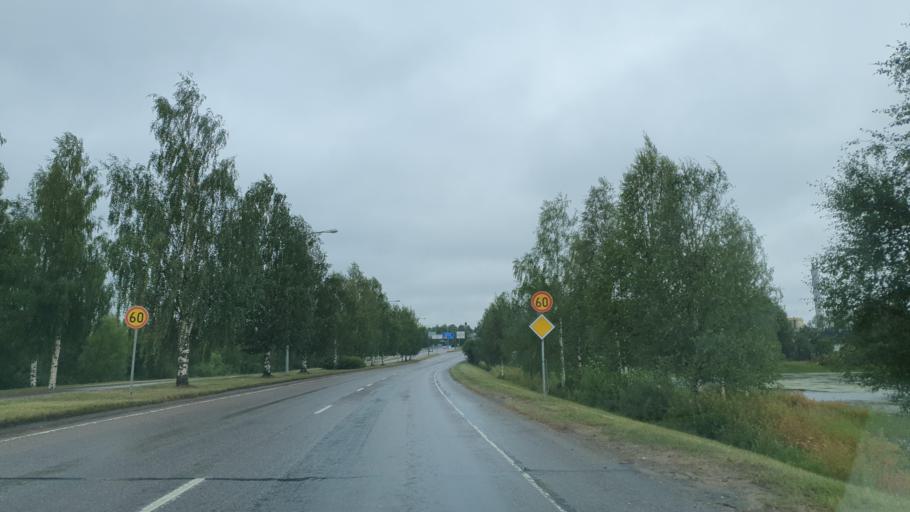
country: FI
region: Lapland
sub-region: Itae-Lappi
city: Kemijaervi
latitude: 66.7191
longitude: 27.4131
